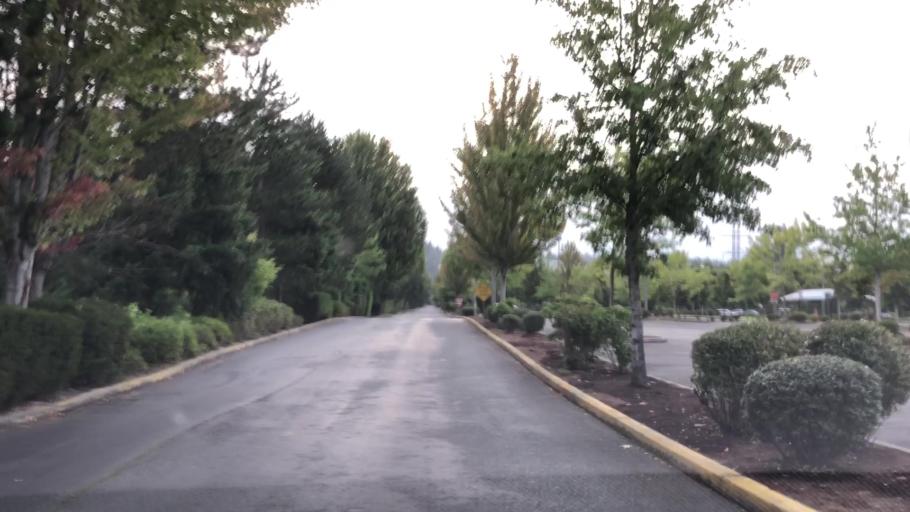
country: US
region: Washington
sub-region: King County
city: Redmond
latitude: 47.6894
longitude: -122.1438
